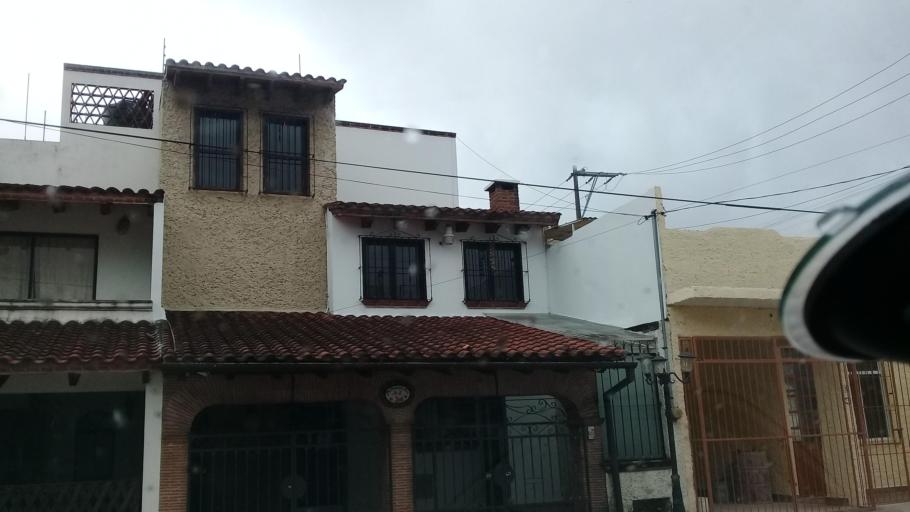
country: MX
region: Veracruz
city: El Castillo
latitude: 19.5328
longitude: -96.8858
